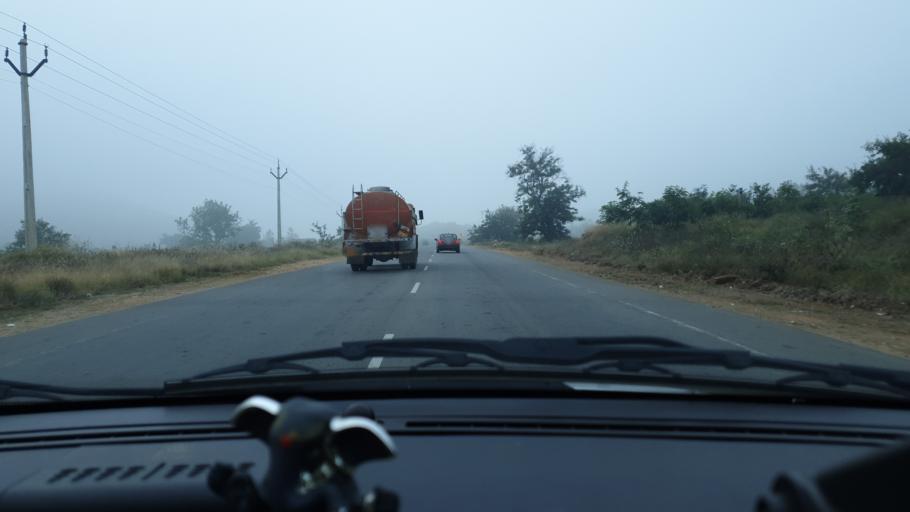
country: IN
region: Telangana
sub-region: Mahbubnagar
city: Farrukhnagar
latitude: 16.9153
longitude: 78.5271
